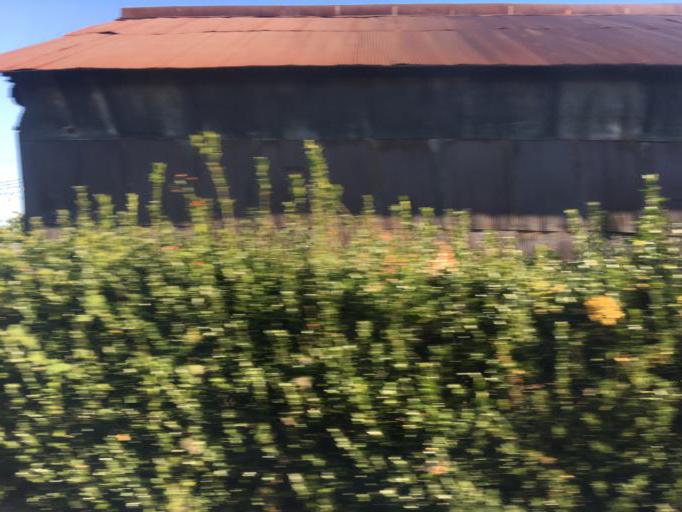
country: JP
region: Gunma
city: Isesaki
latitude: 36.3405
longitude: 139.1675
